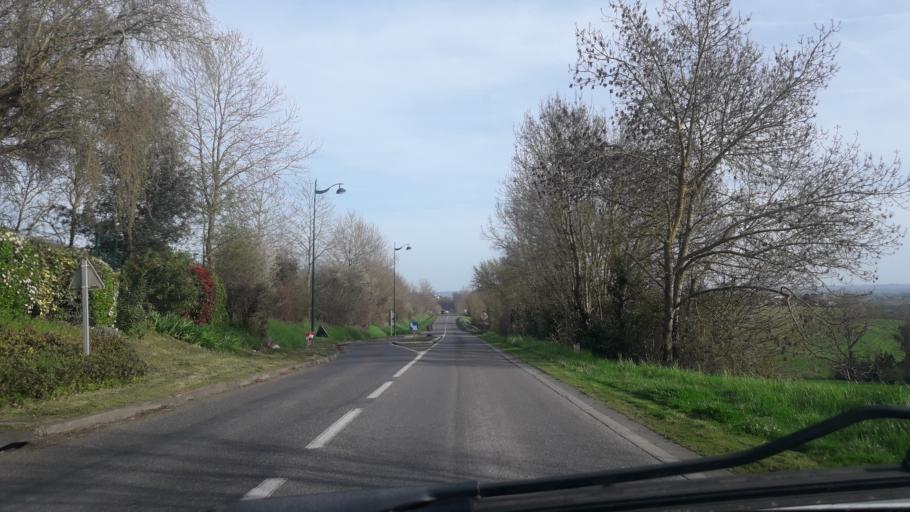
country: FR
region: Midi-Pyrenees
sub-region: Departement du Gers
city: Pujaudran
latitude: 43.6610
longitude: 1.0264
